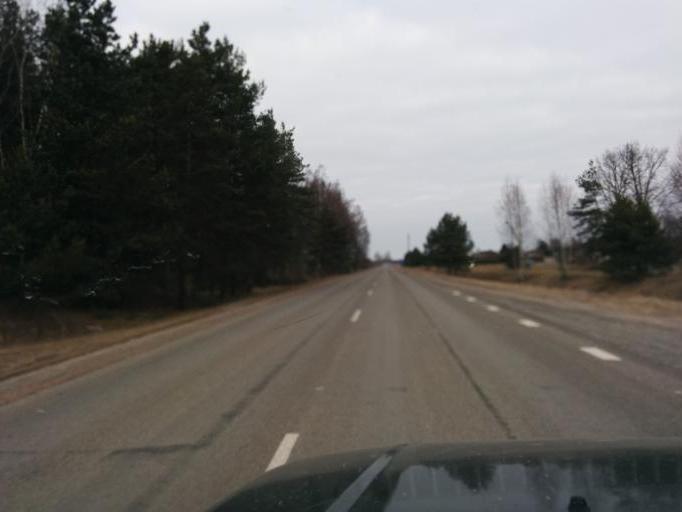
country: LV
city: Tireli
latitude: 56.8367
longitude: 23.5918
